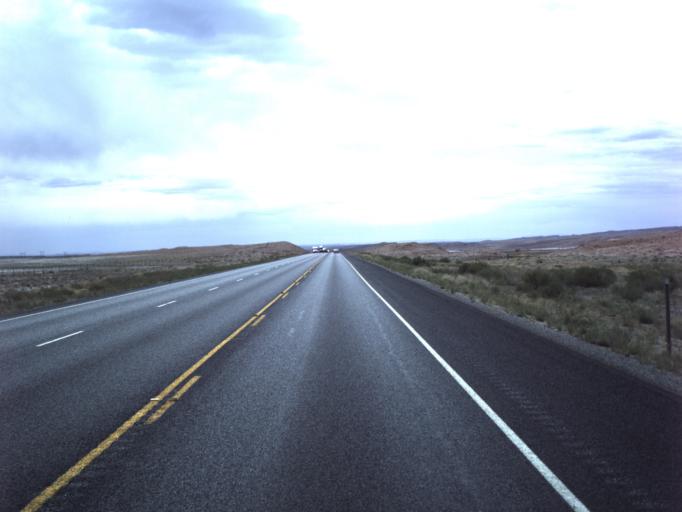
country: US
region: Utah
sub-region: Carbon County
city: East Carbon City
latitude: 39.1519
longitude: -110.3378
